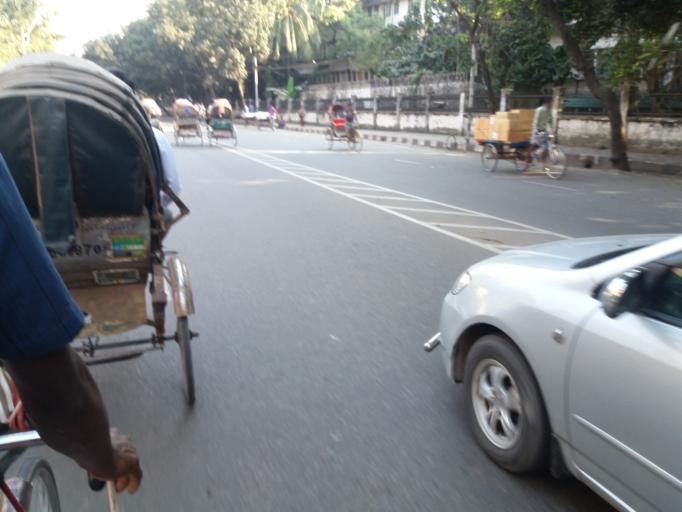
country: BD
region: Dhaka
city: Azimpur
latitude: 23.7254
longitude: 90.3925
